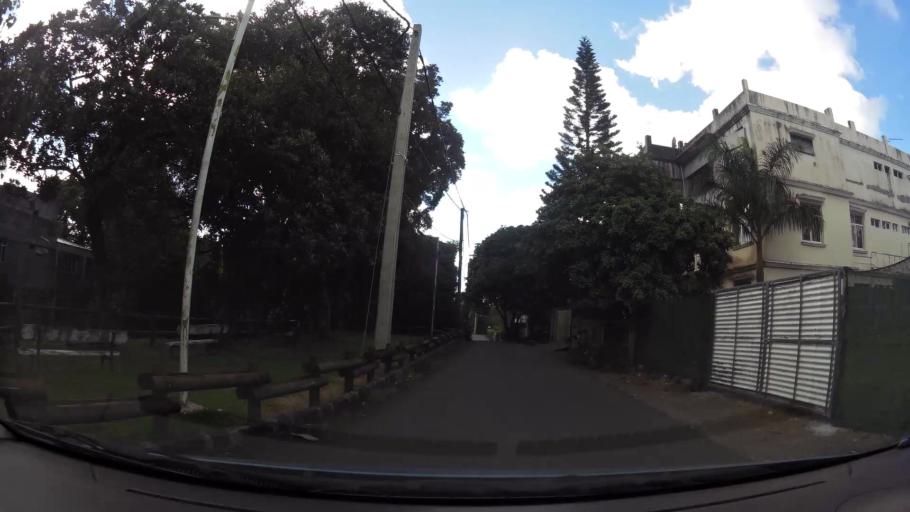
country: MU
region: Plaines Wilhems
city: Curepipe
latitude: -20.2982
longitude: 57.5091
